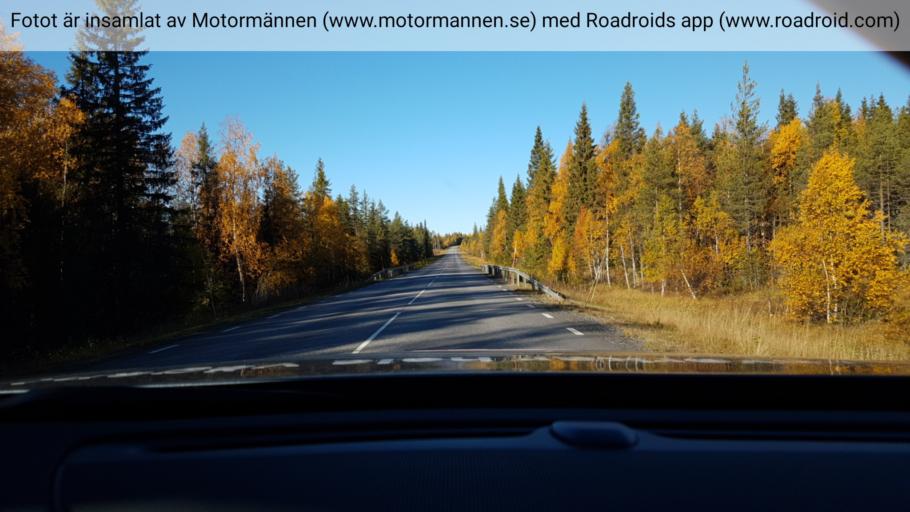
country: SE
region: Vaesterbotten
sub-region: Skelleftea Kommun
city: Storvik
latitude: 65.3371
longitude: 20.5540
